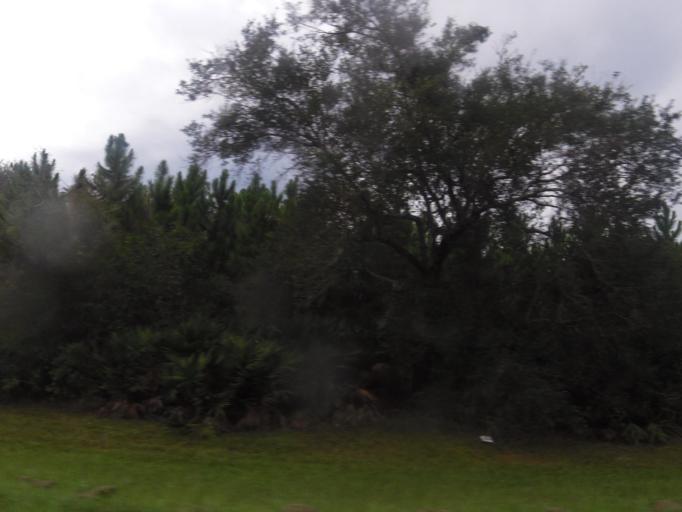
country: US
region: Florida
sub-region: Flagler County
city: Bunnell
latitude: 29.5039
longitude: -81.3358
